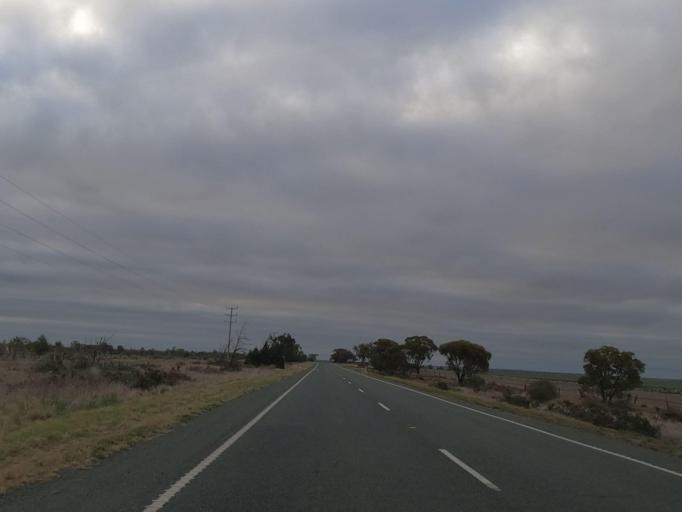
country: AU
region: Victoria
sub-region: Swan Hill
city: Swan Hill
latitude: -35.5726
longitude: 143.7867
